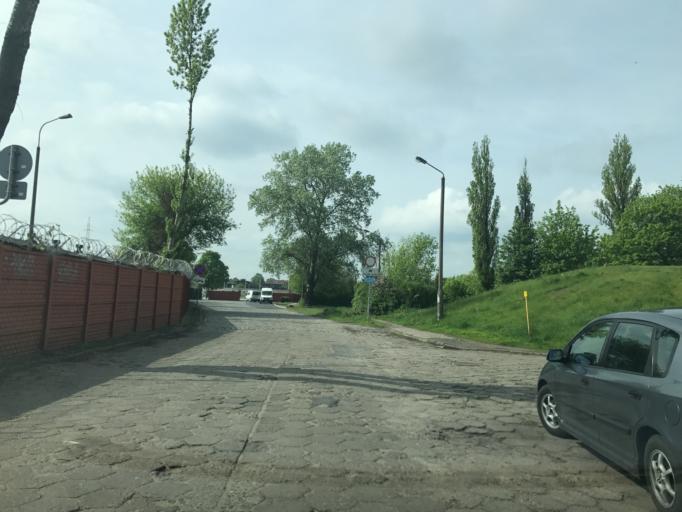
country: PL
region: Kujawsko-Pomorskie
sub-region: Bydgoszcz
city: Bydgoszcz
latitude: 53.1412
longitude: 18.0101
